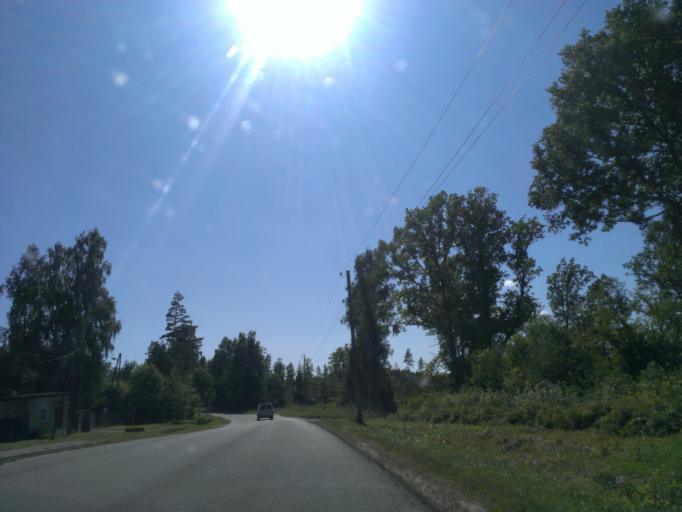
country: LV
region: Sigulda
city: Sigulda
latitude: 57.1253
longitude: 24.8293
